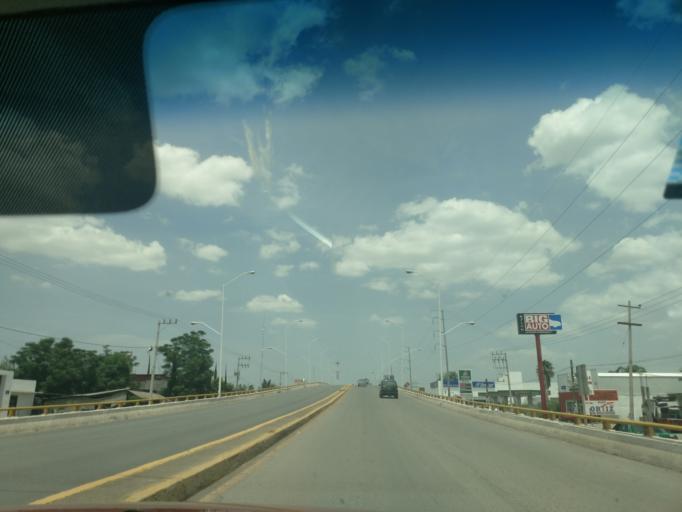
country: MX
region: San Luis Potosi
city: Rio Verde
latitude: 21.9234
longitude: -99.9964
